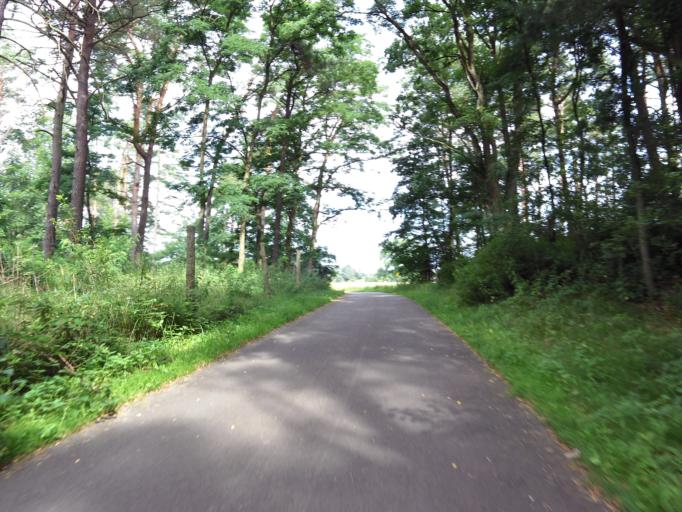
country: DE
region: Brandenburg
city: Lychen
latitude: 53.2792
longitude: 13.3047
